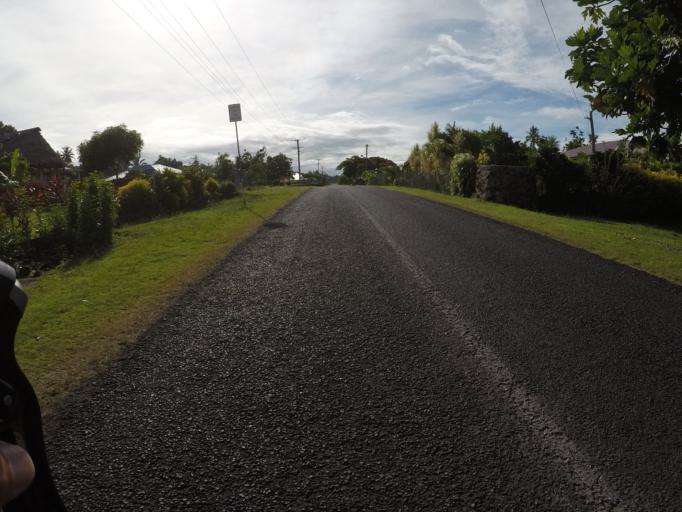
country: WS
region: Vaisigano
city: Asau
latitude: -13.6827
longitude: -172.6240
